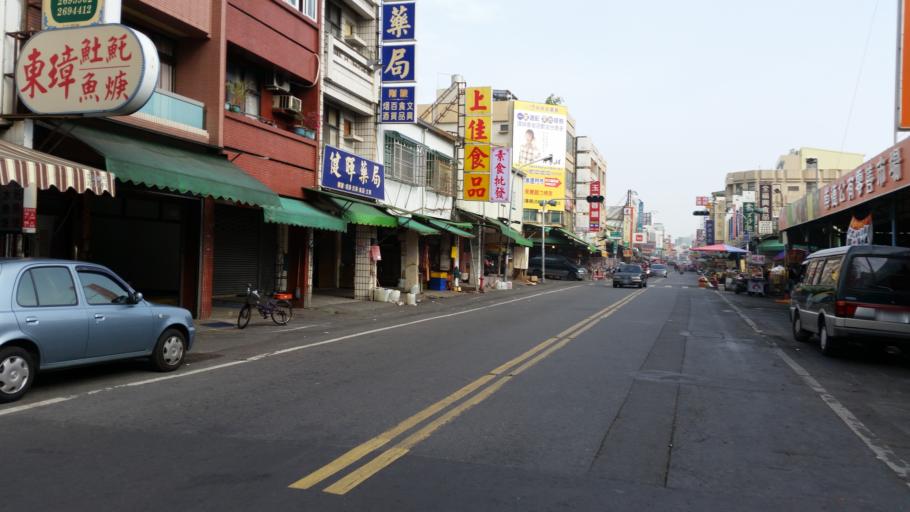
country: TW
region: Taiwan
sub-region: Tainan
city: Tainan
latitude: 22.9773
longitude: 120.2226
